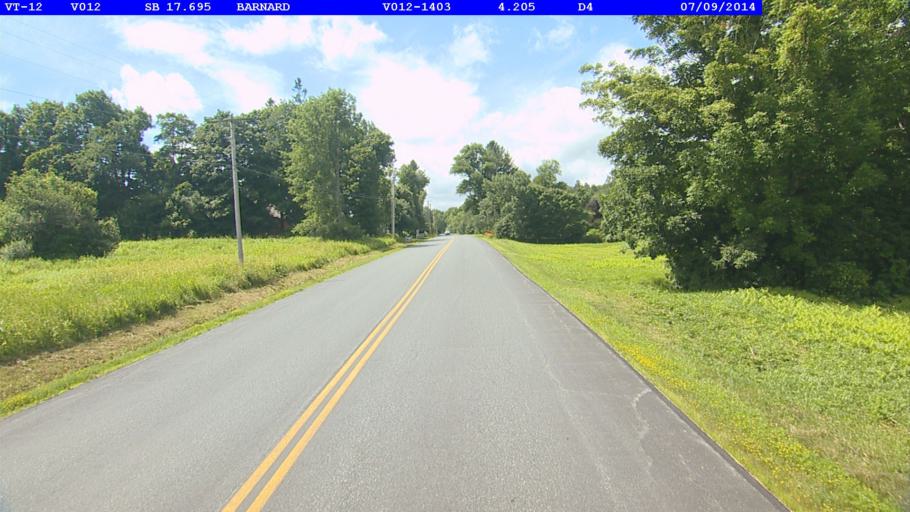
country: US
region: Vermont
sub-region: Windsor County
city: Woodstock
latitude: 43.7211
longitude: -72.6218
